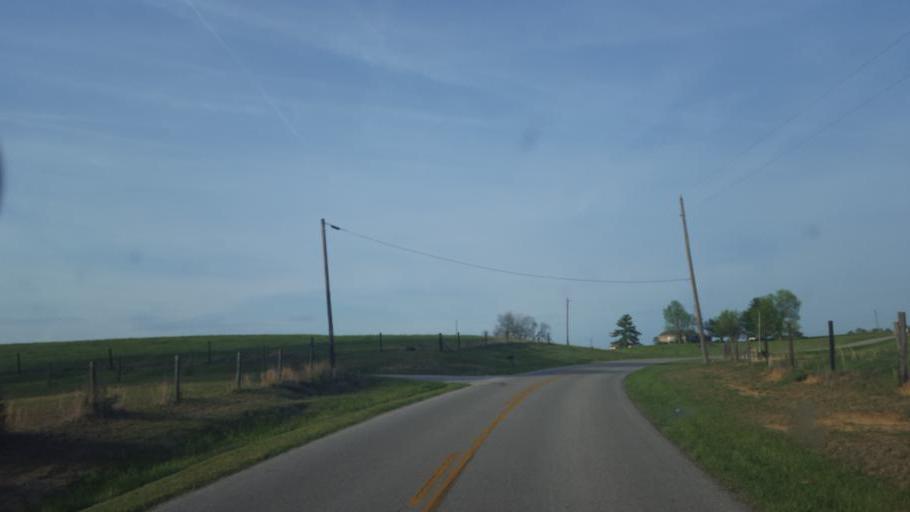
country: US
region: Kentucky
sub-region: Allen County
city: Scottsville
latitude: 36.9060
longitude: -86.1210
